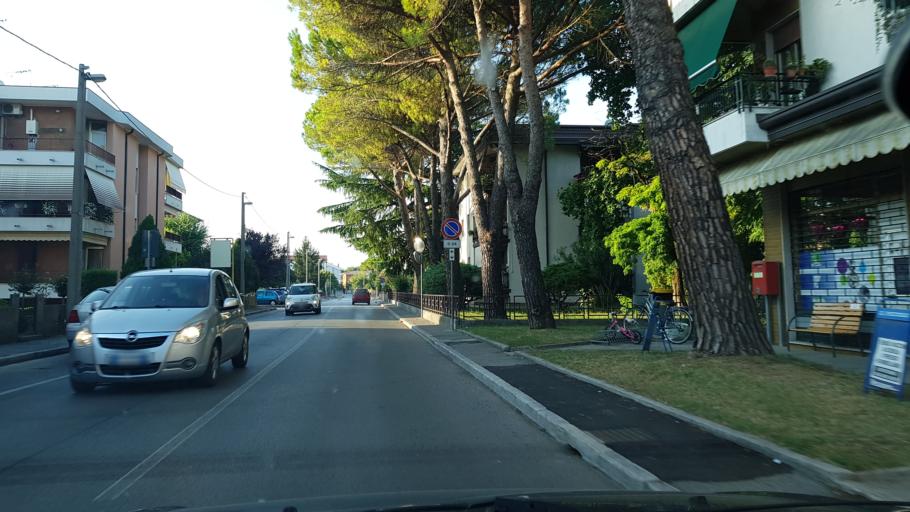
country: IT
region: Friuli Venezia Giulia
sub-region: Provincia di Gorizia
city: Staranzano
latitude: 45.7991
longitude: 13.5066
